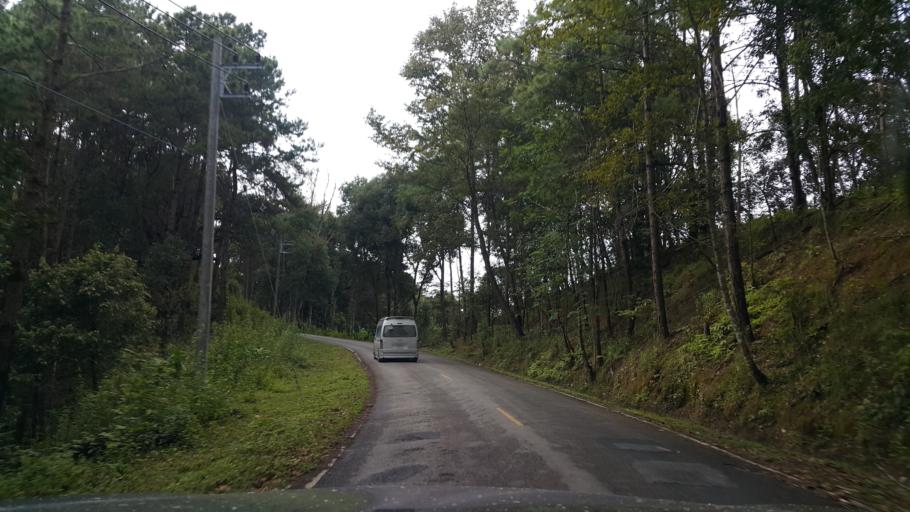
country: TH
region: Chiang Mai
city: Chaem Luang
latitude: 18.9204
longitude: 98.4772
